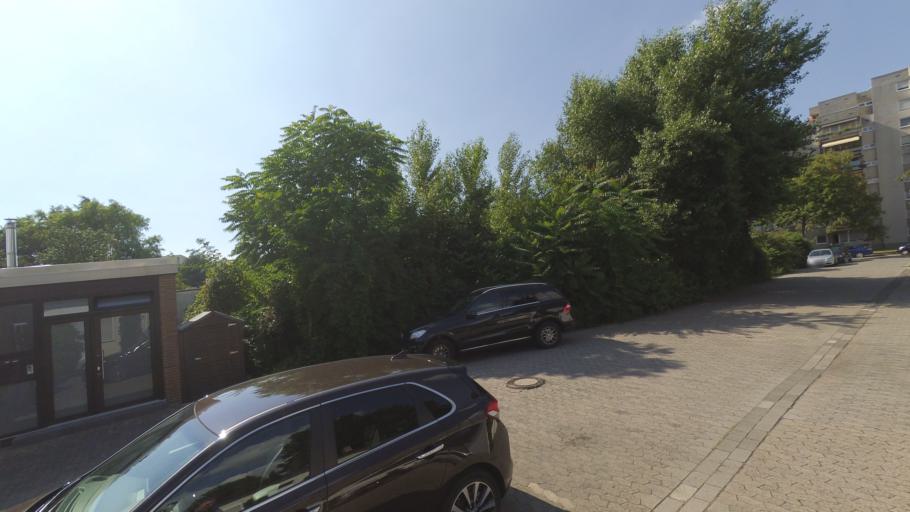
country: DE
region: Rheinland-Pfalz
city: Gartenstadt
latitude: 49.4908
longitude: 8.3964
